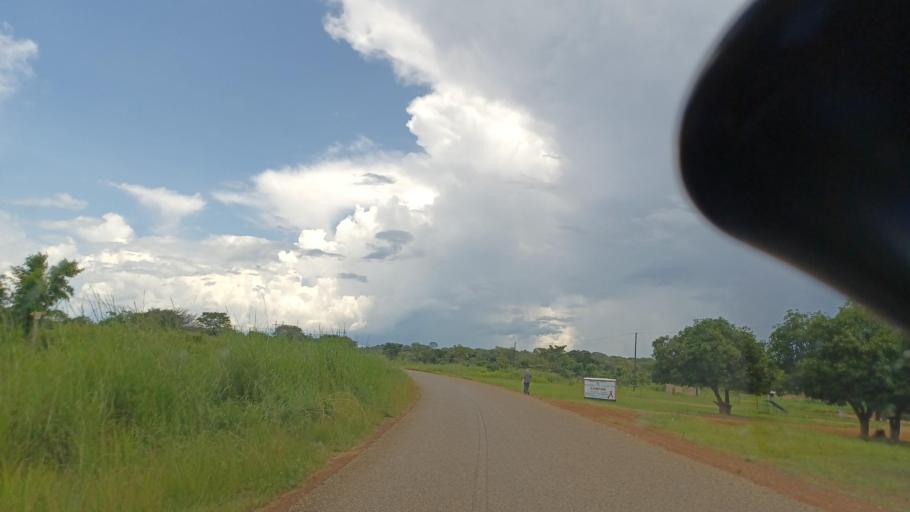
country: ZM
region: North-Western
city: Kasempa
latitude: -12.8648
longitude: 26.0379
